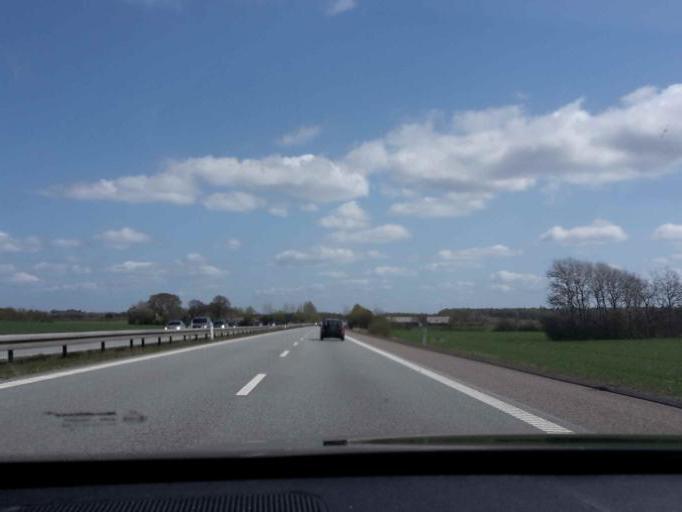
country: DK
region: South Denmark
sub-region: Vejen Kommune
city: Brorup
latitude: 55.5032
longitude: 9.0381
